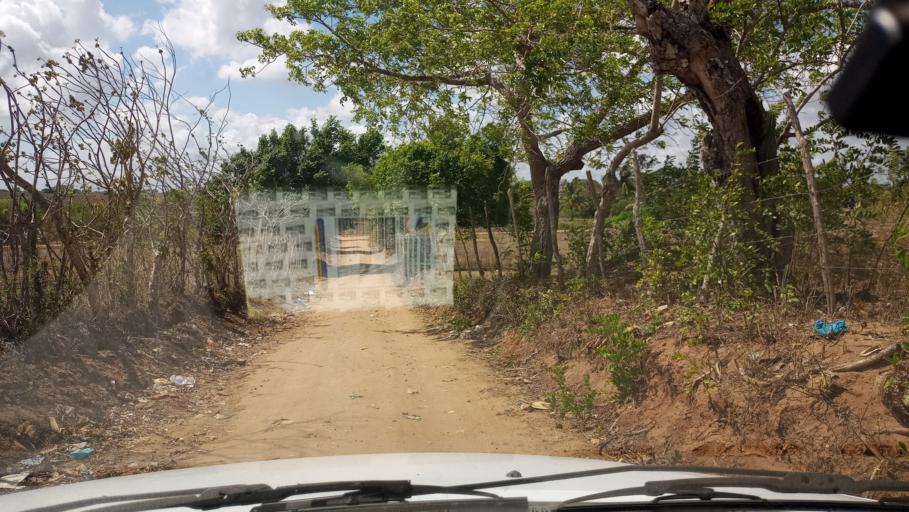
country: BR
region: Rio Grande do Norte
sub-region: Santo Antonio
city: Santo Antonio
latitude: -6.3473
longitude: -35.3701
